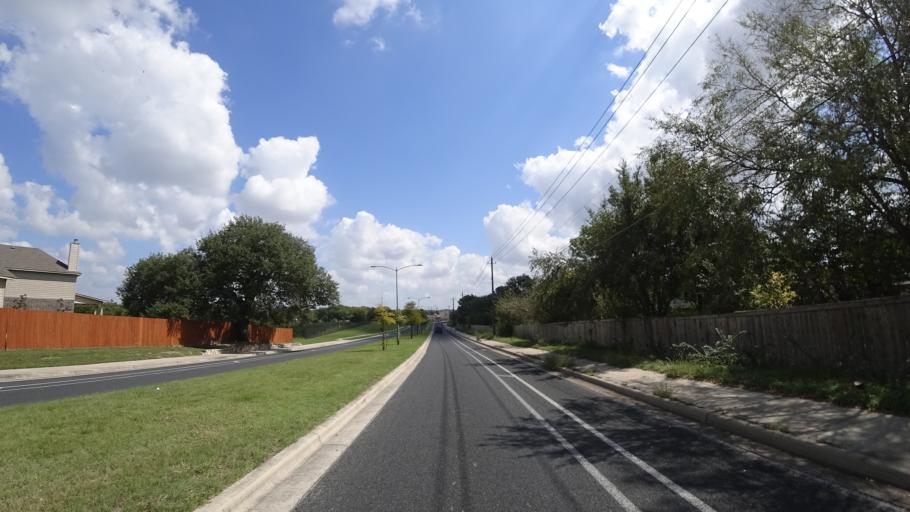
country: US
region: Texas
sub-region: Travis County
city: Onion Creek
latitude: 30.1856
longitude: -97.7978
